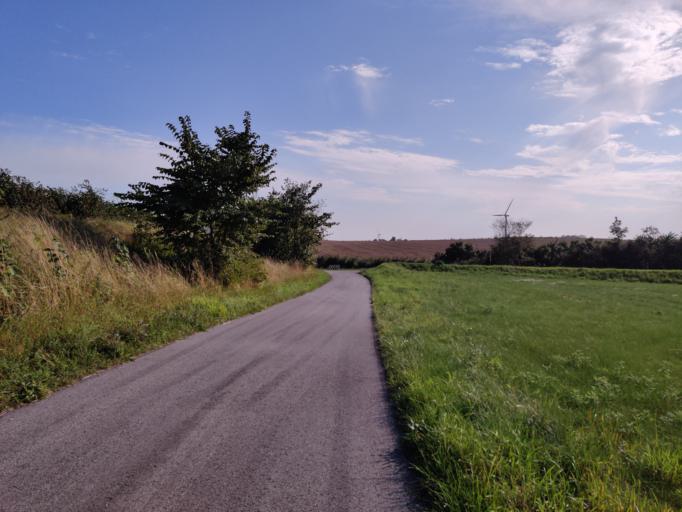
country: DK
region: Zealand
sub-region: Guldborgsund Kommune
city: Nykobing Falster
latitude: 54.6849
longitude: 11.9003
